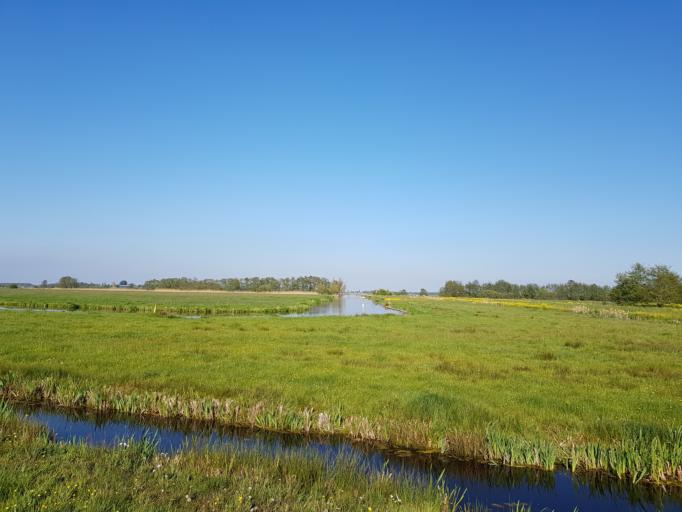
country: NL
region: South Holland
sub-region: Gemeente Vlist
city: Haastrecht
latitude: 51.9449
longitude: 4.7384
